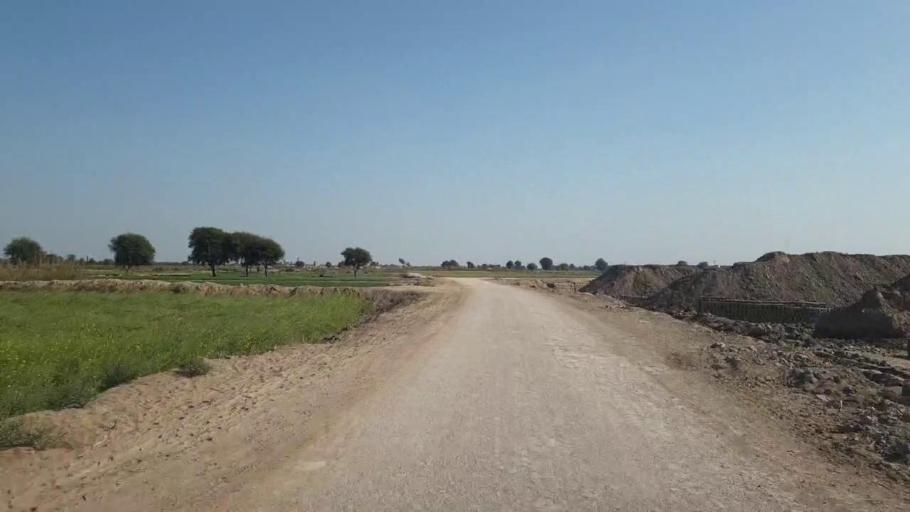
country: PK
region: Sindh
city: Tando Allahyar
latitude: 25.4107
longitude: 68.7046
